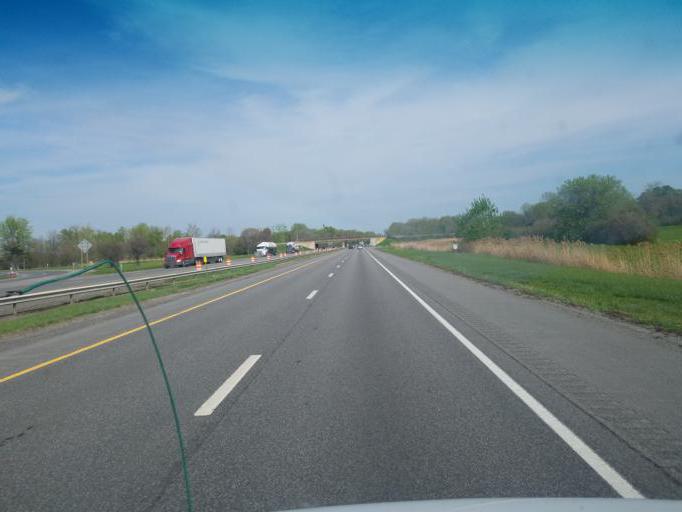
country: US
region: New York
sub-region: Onondaga County
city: Liverpool
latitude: 43.1169
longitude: -76.2180
